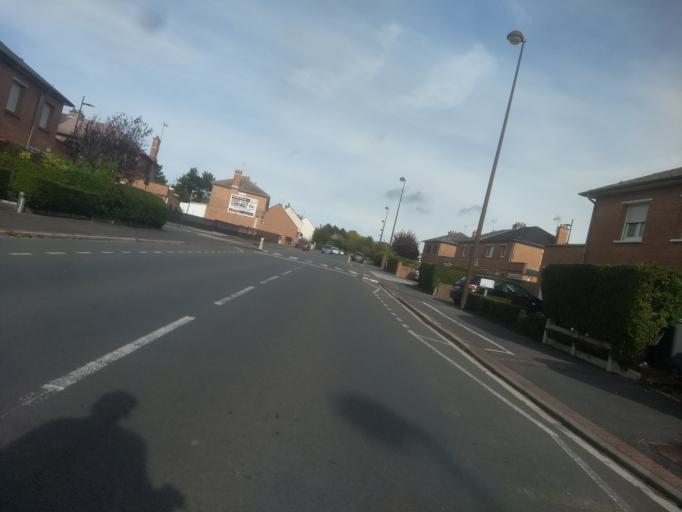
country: FR
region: Nord-Pas-de-Calais
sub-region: Departement du Pas-de-Calais
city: Dainville
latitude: 50.2901
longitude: 2.7421
